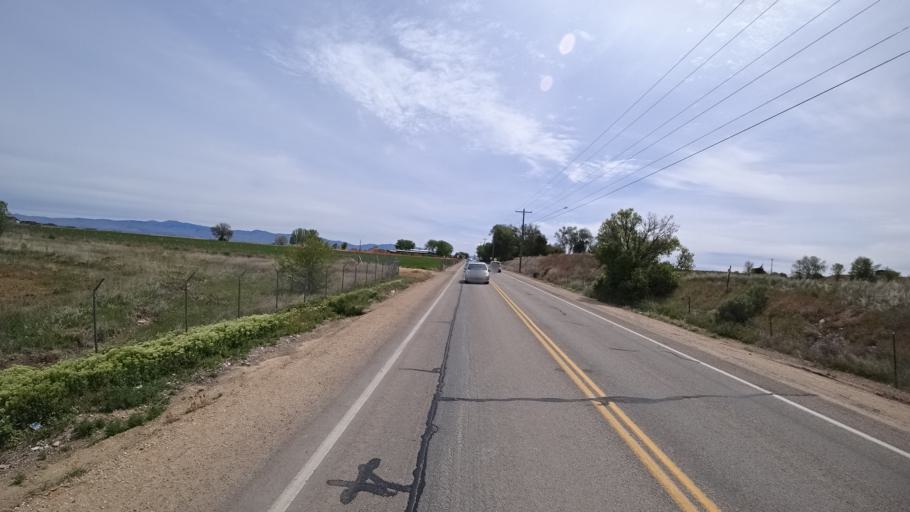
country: US
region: Idaho
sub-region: Ada County
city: Meridian
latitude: 43.5611
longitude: -116.3862
